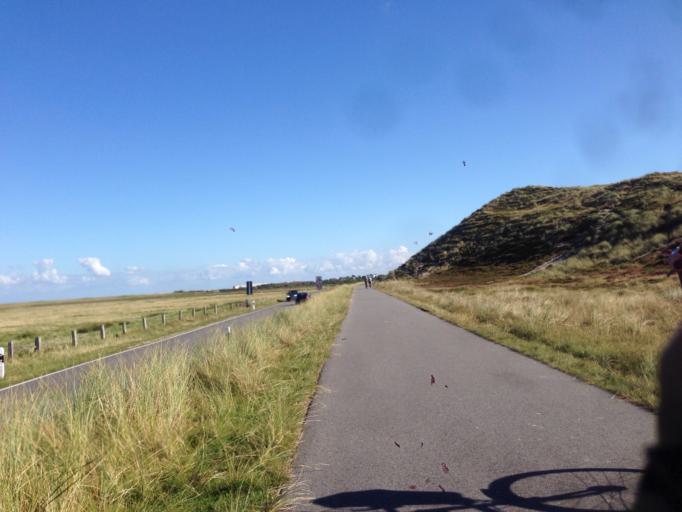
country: DE
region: Schleswig-Holstein
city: List
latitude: 55.0297
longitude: 8.4159
